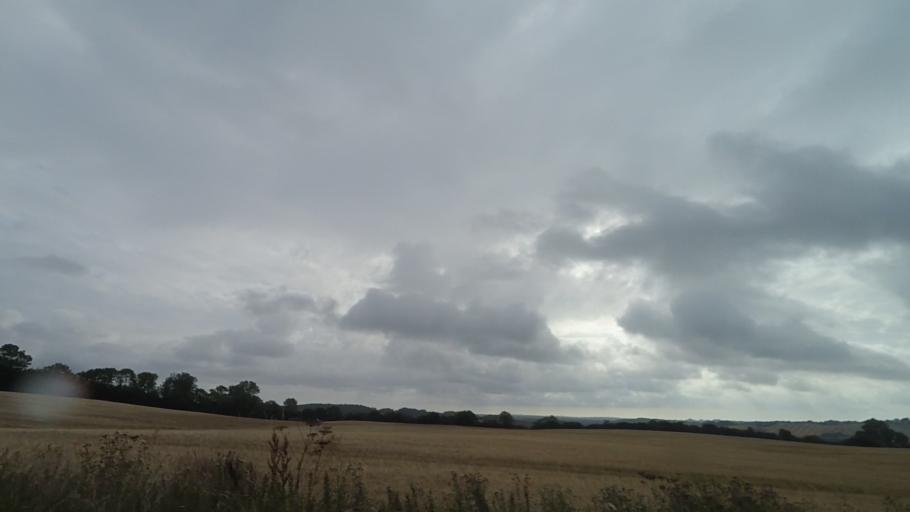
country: DK
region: Central Jutland
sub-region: Syddjurs Kommune
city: Ronde
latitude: 56.3217
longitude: 10.4592
